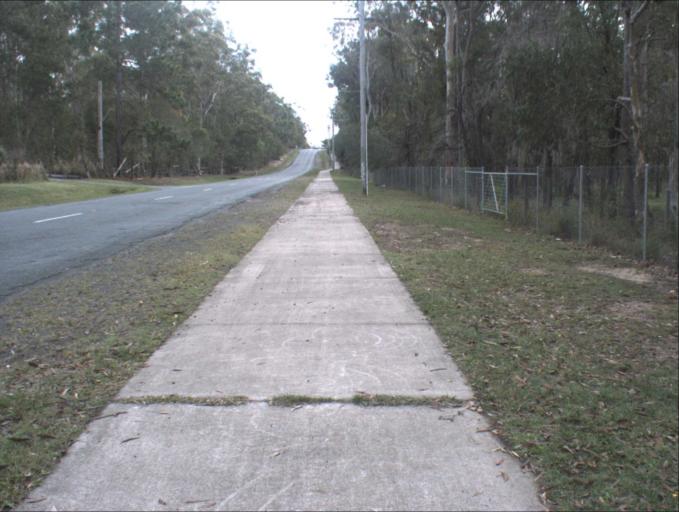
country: AU
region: Queensland
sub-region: Logan
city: Logan Reserve
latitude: -27.6999
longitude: 153.0767
